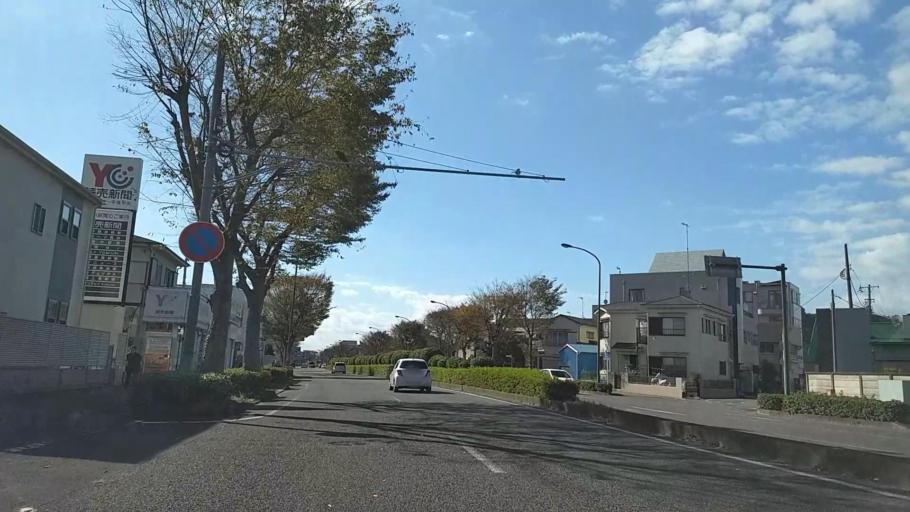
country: JP
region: Kanagawa
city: Hiratsuka
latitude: 35.3286
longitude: 139.3338
